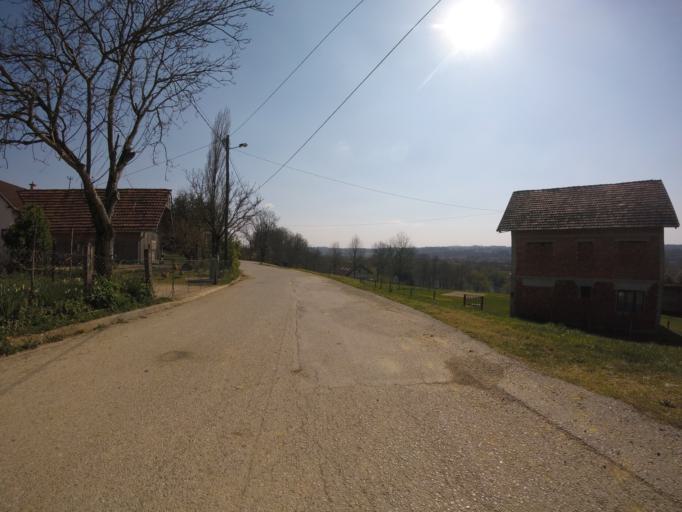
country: HR
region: Sisacko-Moslavacka
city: Gvozd
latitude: 45.5137
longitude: 15.9235
